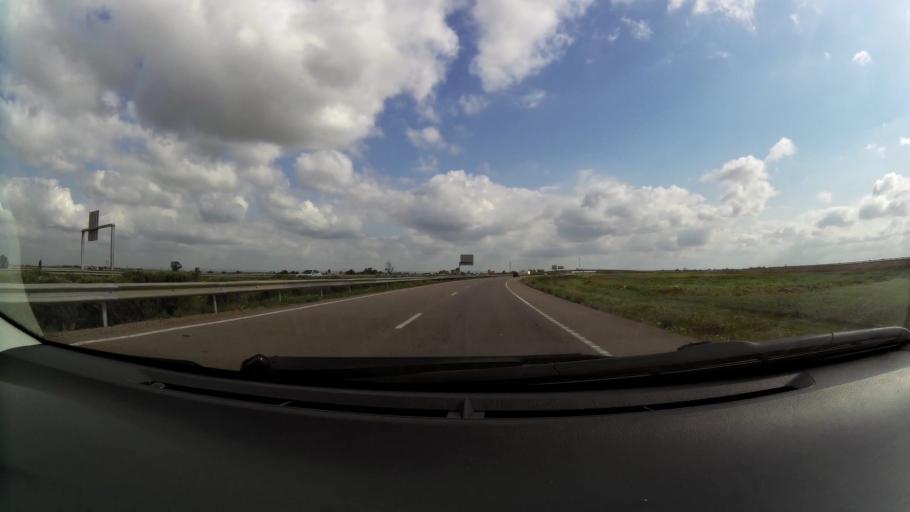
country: MA
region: Chaouia-Ouardigha
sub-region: Settat Province
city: Berrechid
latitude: 33.2870
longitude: -7.5473
